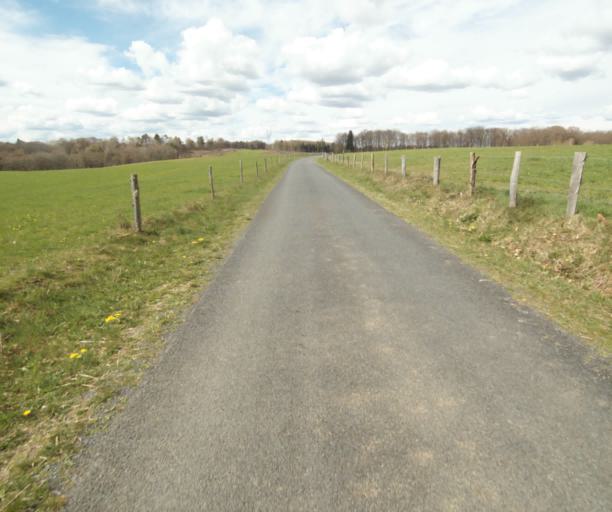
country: FR
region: Limousin
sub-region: Departement de la Correze
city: Argentat
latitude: 45.2000
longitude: 1.9077
